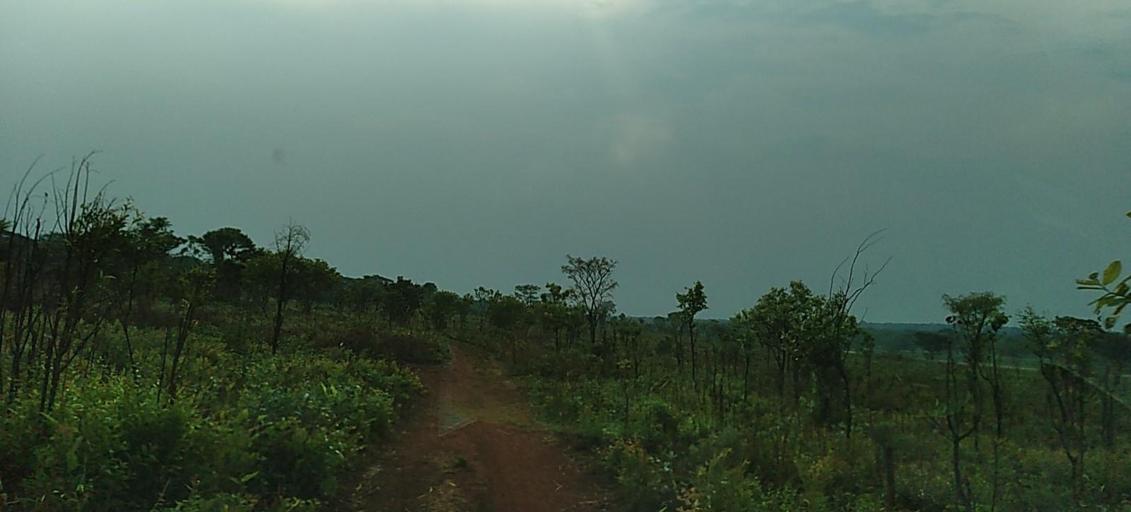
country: ZM
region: North-Western
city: Solwezi
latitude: -12.0430
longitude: 26.0283
